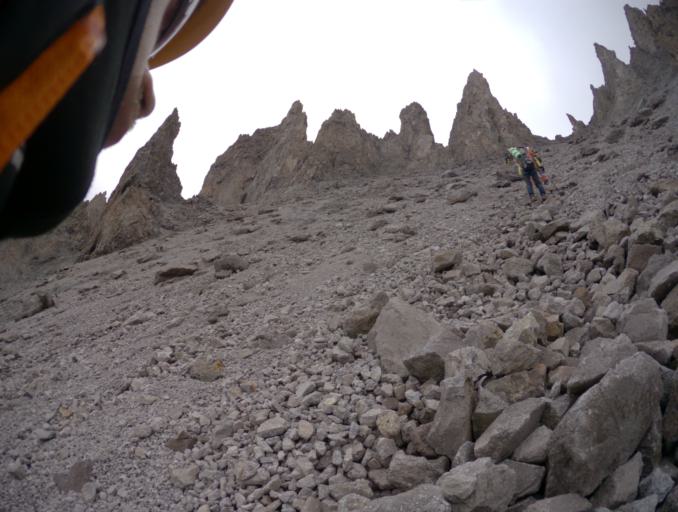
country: RU
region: Kabardino-Balkariya
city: Terskol
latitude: 43.3786
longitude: 42.4052
